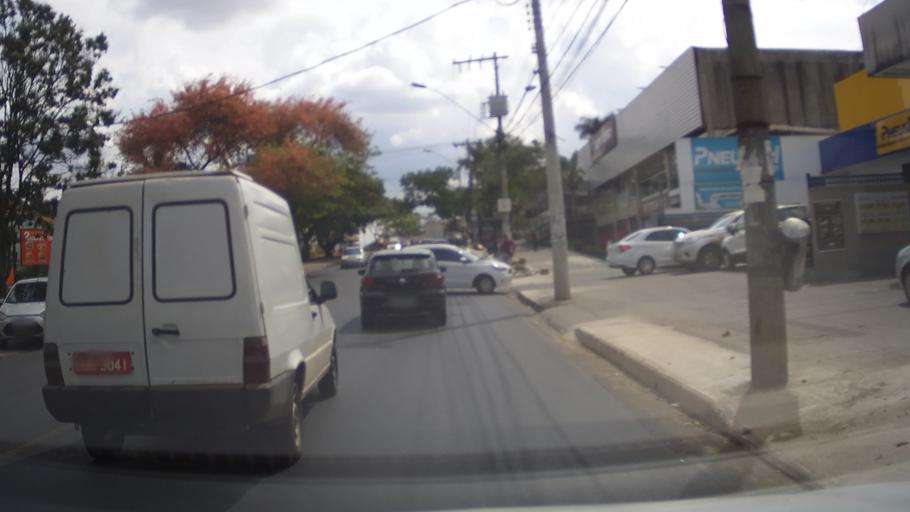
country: BR
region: Minas Gerais
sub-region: Belo Horizonte
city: Belo Horizonte
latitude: -19.8458
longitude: -43.9729
